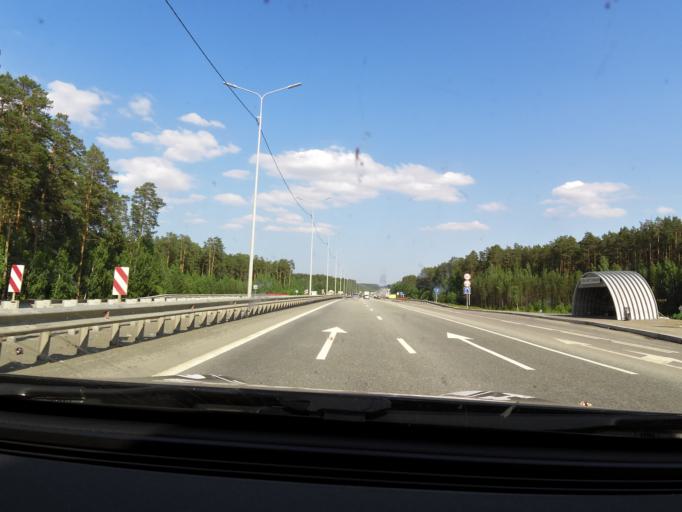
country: RU
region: Sverdlovsk
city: Severka
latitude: 56.8313
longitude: 60.3887
